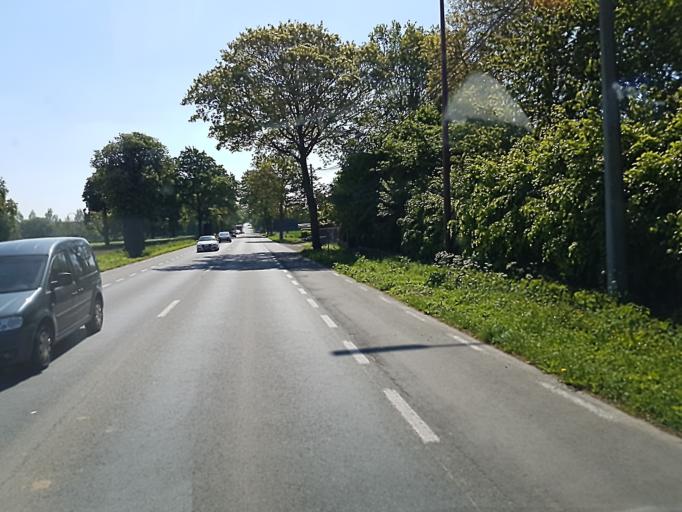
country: BE
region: Wallonia
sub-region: Province du Hainaut
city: Chievres
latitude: 50.6080
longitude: 3.8055
